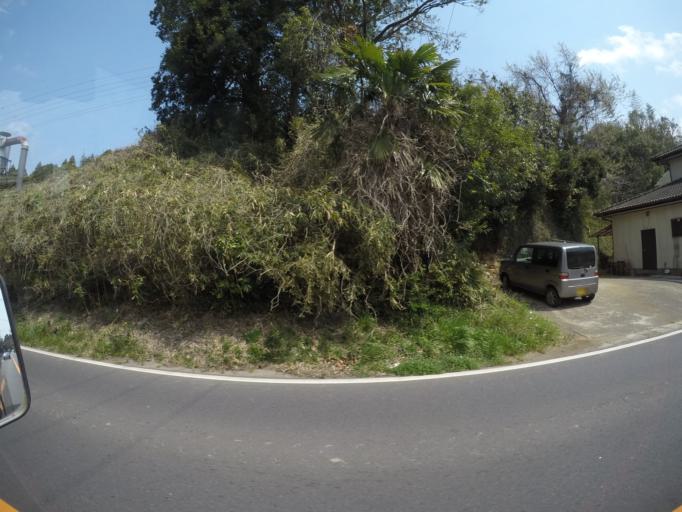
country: JP
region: Chiba
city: Sawara
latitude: 35.8769
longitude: 140.5340
